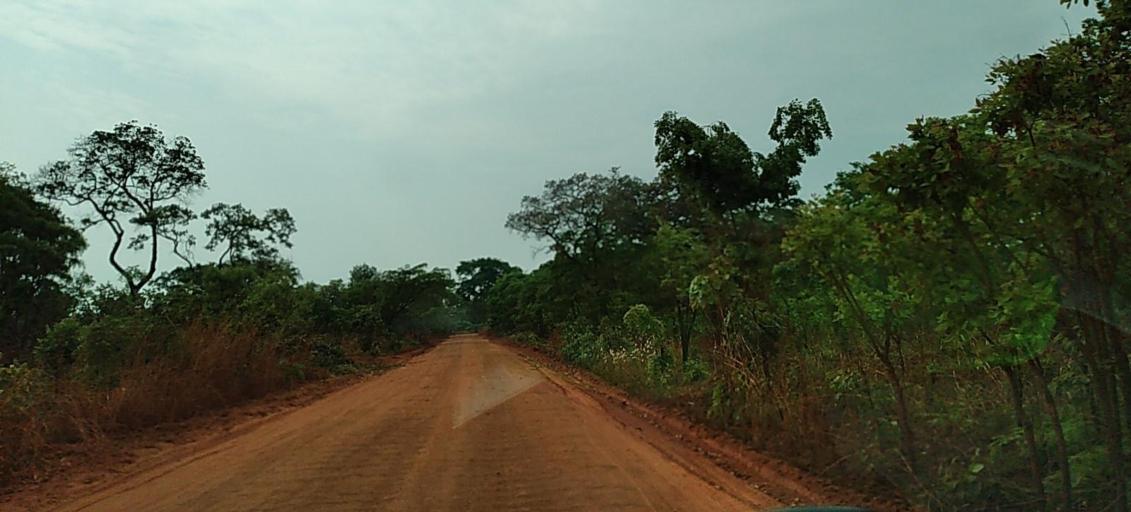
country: ZM
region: North-Western
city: Solwezi
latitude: -12.2158
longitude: 26.5067
